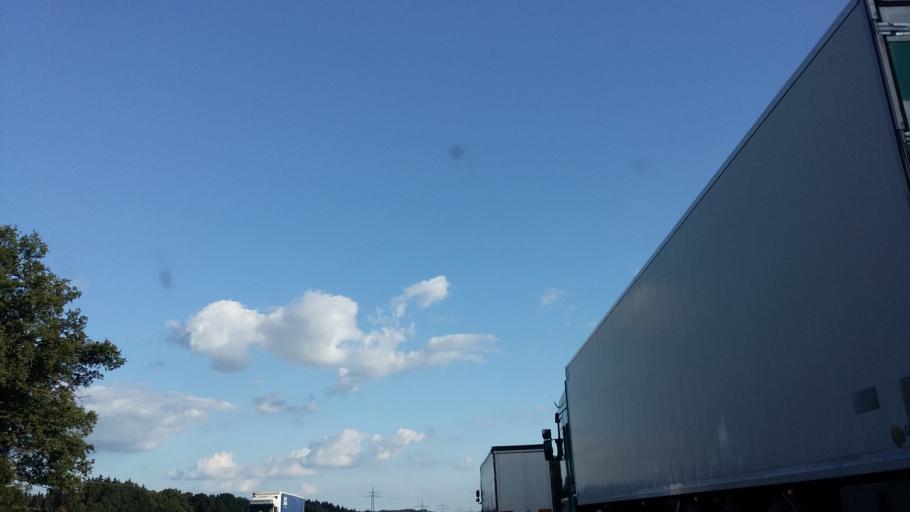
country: DE
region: Bavaria
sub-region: Swabia
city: Vohringen
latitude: 48.3073
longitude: 10.0999
